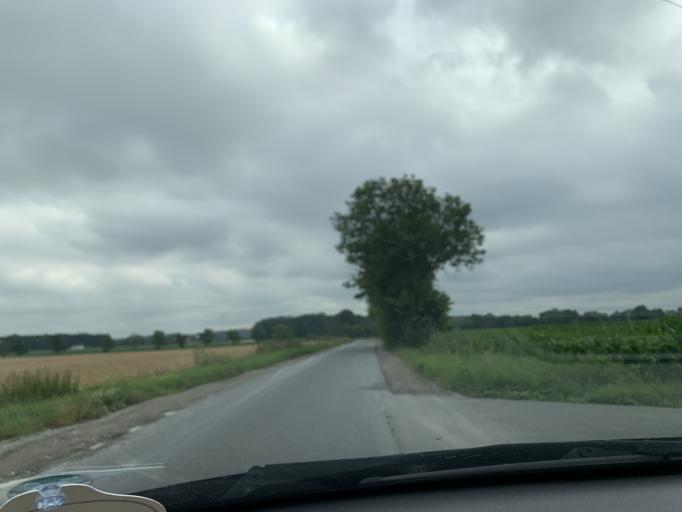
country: DE
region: North Rhine-Westphalia
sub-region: Regierungsbezirk Munster
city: Ennigerloh
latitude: 51.8397
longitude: 8.0765
